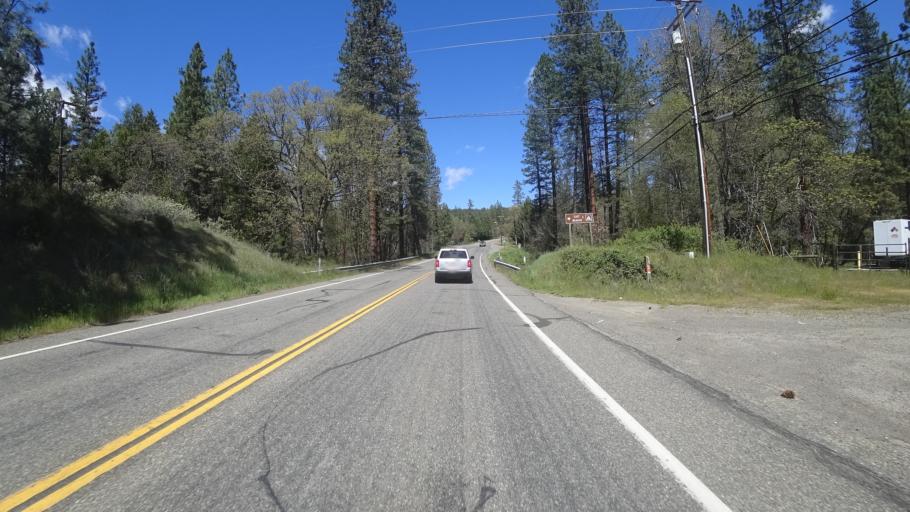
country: US
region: California
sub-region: Trinity County
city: Weaverville
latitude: 40.7498
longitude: -122.9195
